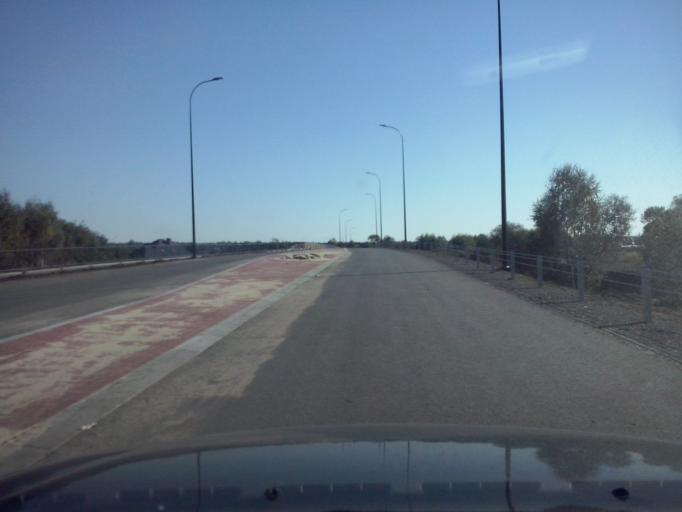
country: PL
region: Lublin Voivodeship
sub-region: Powiat bilgorajski
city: Bilgoraj
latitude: 50.5217
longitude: 22.7099
